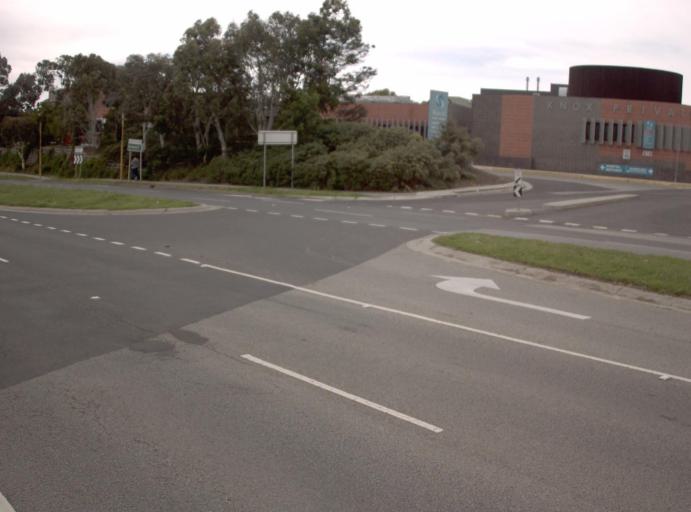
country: AU
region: Victoria
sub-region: Knox
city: Wantirna
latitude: -37.8492
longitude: 145.2265
